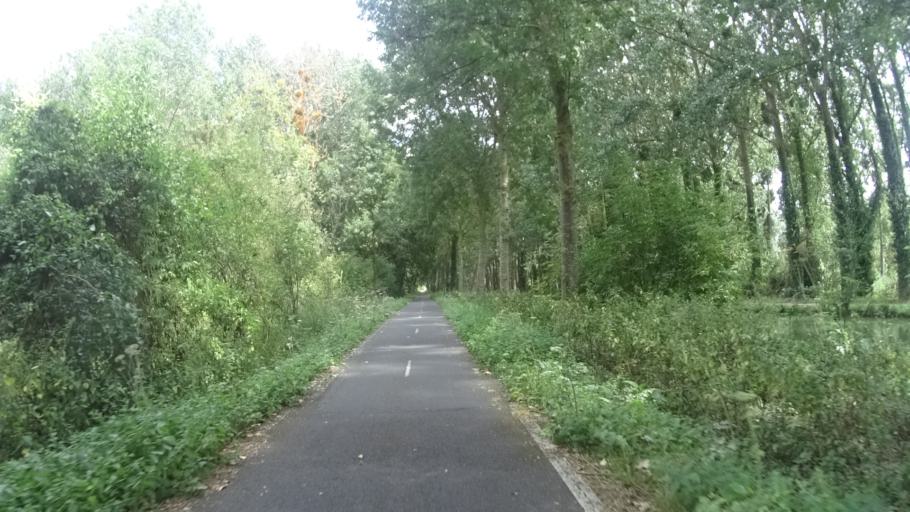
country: FR
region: Ile-de-France
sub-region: Departement de Seine-et-Marne
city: Claye-Souilly
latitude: 48.9562
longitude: 2.6574
